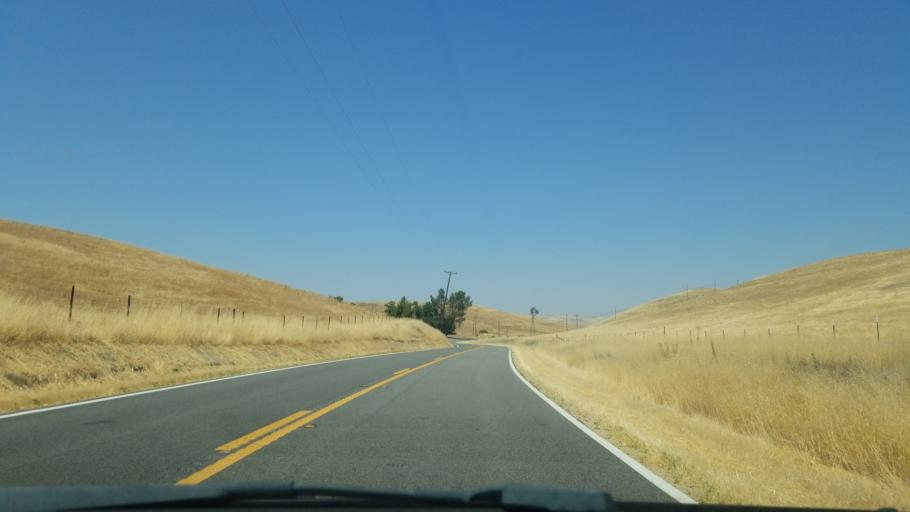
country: US
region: California
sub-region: San Luis Obispo County
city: Shandon
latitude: 35.6124
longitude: -120.4061
